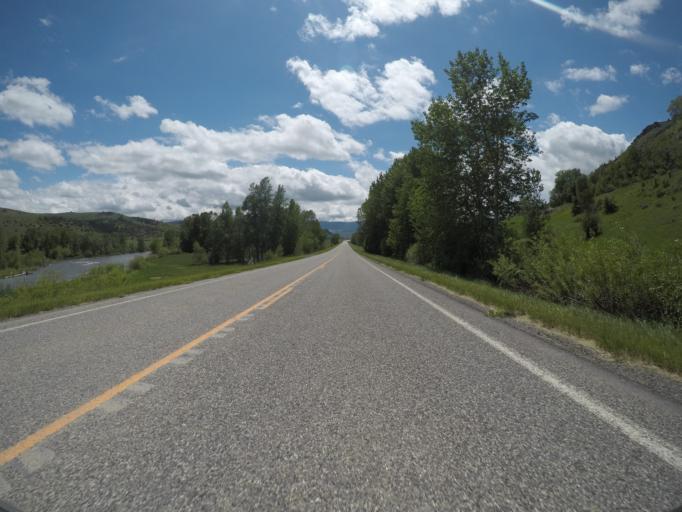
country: US
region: Montana
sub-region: Sweet Grass County
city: Big Timber
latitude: 45.6532
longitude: -110.1142
